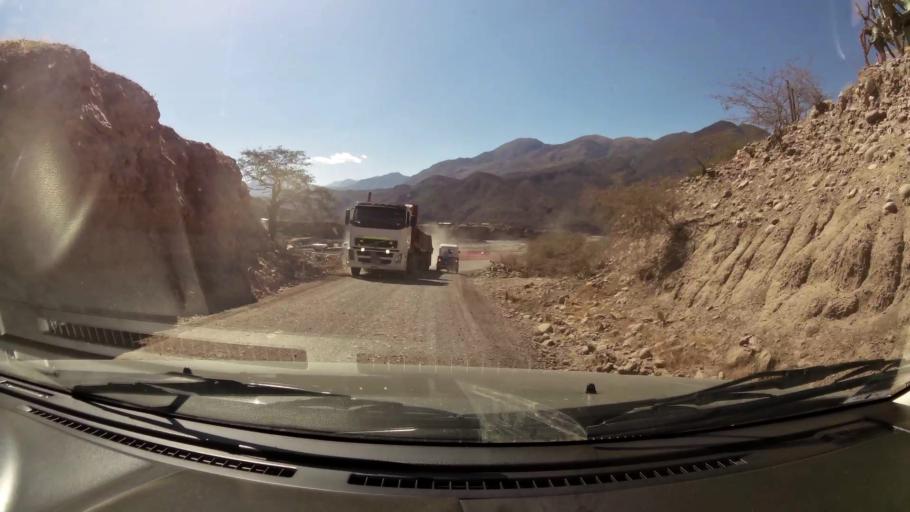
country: PE
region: Huancavelica
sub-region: Provincia de Acobamba
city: Marcas
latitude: -12.8494
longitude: -74.3324
